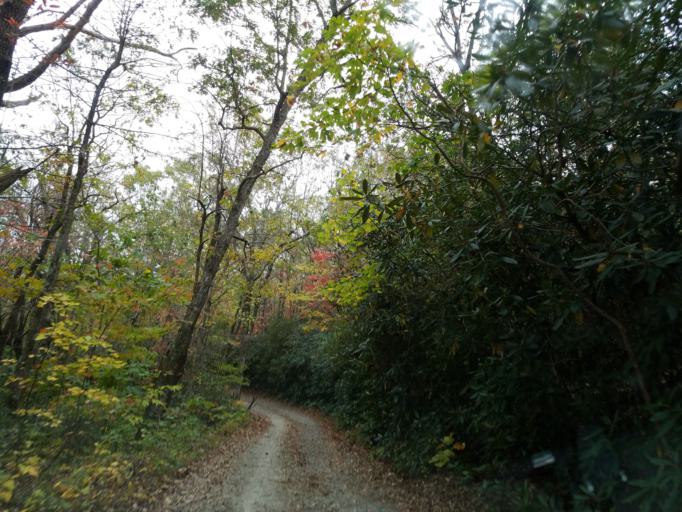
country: US
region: Georgia
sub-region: Dawson County
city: Dawsonville
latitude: 34.5943
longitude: -84.2222
